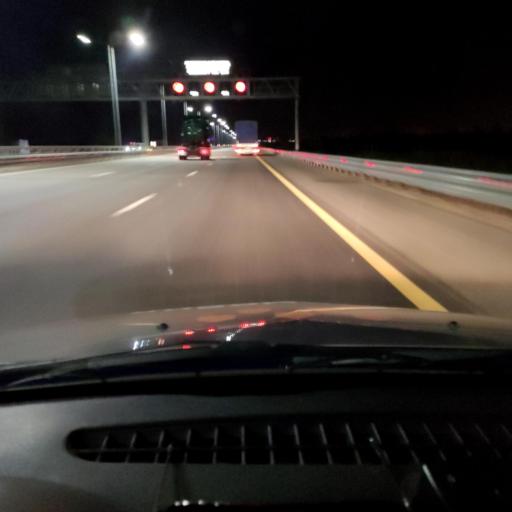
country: RU
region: Voronezj
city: Somovo
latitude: 51.7743
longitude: 39.3003
